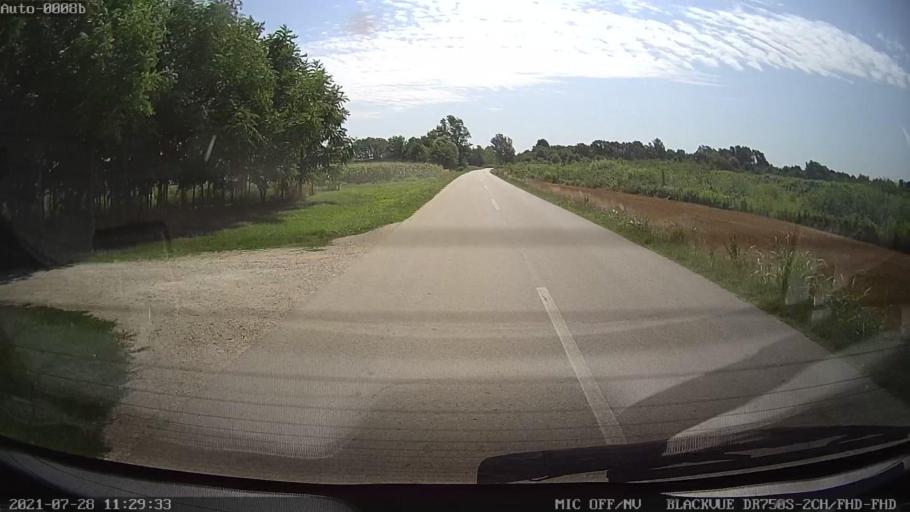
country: HR
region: Medimurska
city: Kursanec
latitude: 46.2791
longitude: 16.4204
